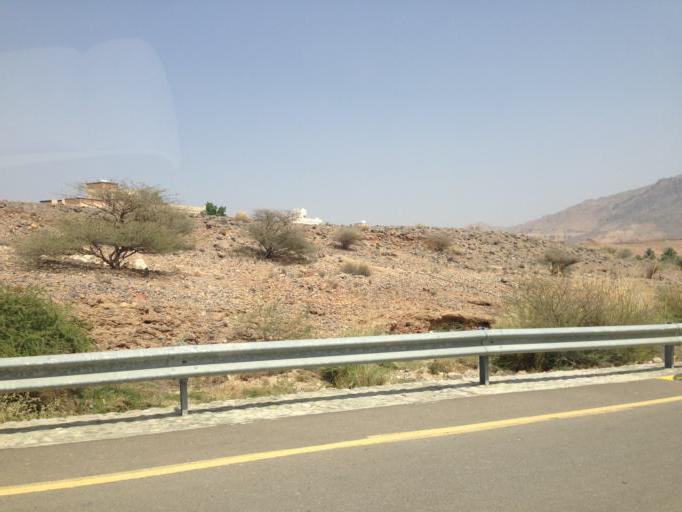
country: OM
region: Ash Sharqiyah
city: Ibra'
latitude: 23.0893
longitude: 58.8519
